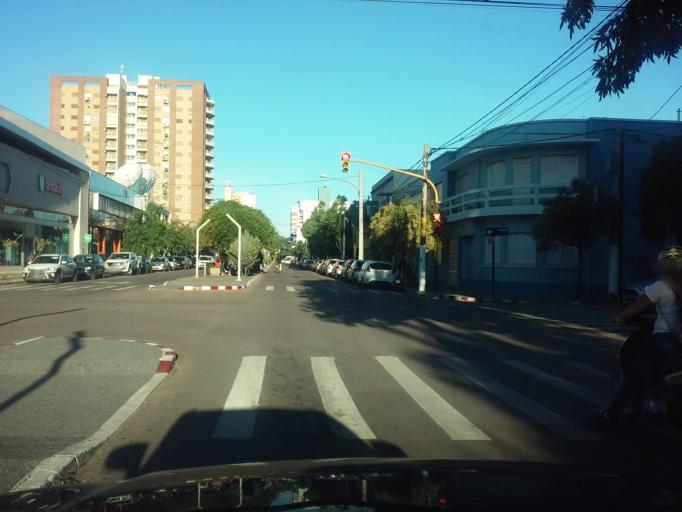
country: AR
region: La Pampa
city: Santa Rosa
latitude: -36.6210
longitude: -64.2875
